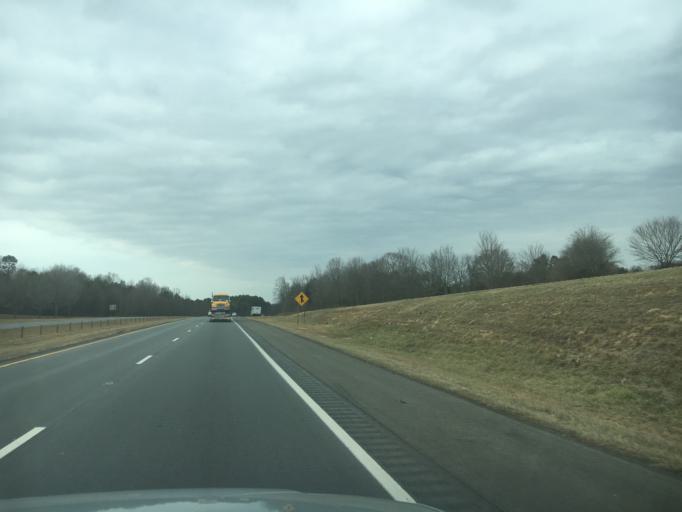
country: US
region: North Carolina
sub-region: Catawba County
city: Maiden
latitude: 35.5286
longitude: -81.2230
